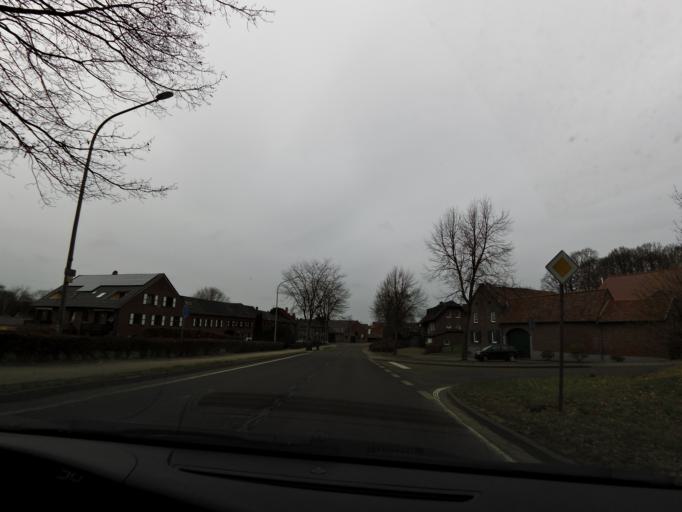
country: DE
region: North Rhine-Westphalia
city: Geilenkirchen
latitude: 50.9680
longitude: 6.0780
